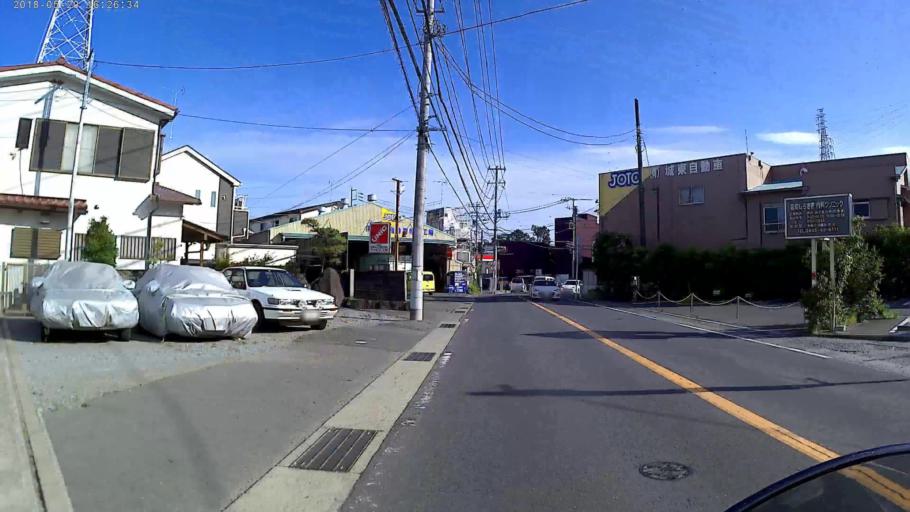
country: JP
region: Kanagawa
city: Odawara
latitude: 35.2765
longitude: 139.1552
